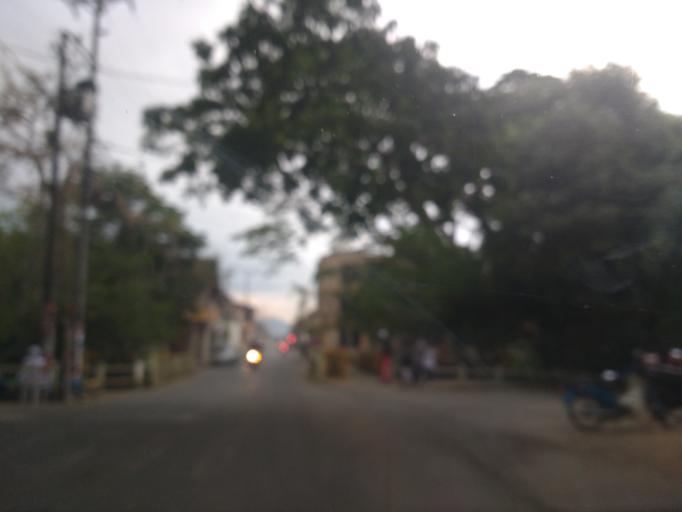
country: CO
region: Cauca
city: Santander de Quilichao
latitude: 3.0046
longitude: -76.4805
